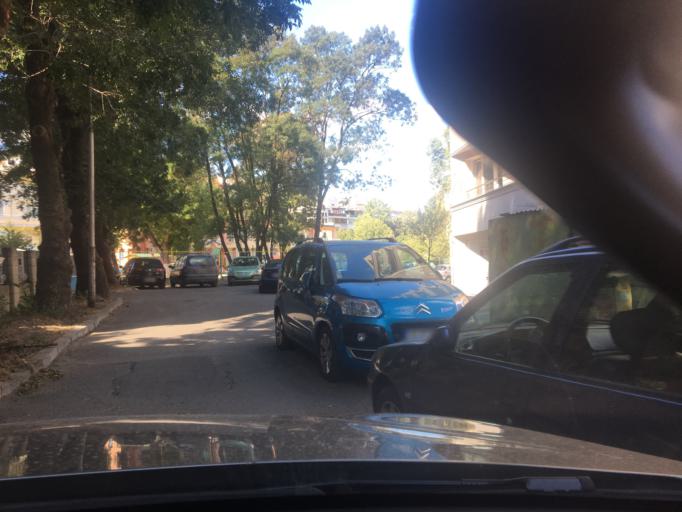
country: BG
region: Burgas
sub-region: Obshtina Burgas
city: Burgas
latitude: 42.5096
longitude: 27.4719
